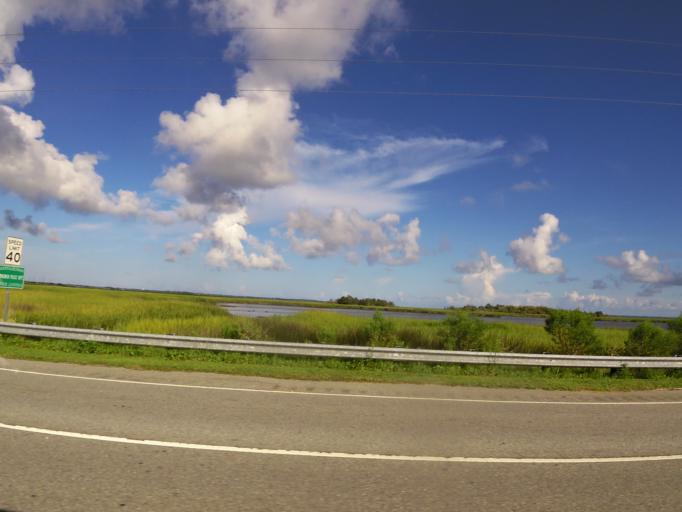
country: US
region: Georgia
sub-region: Glynn County
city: Brunswick
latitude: 31.1579
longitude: -81.4786
